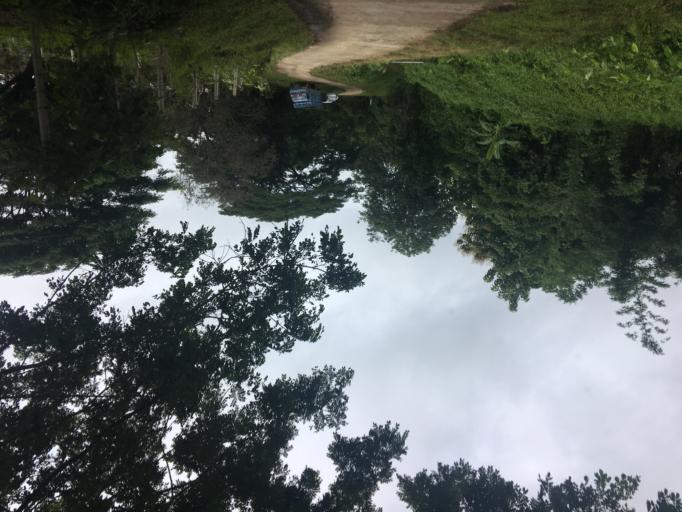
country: TH
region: Chiang Rai
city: Mae Lao
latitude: 19.6926
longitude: 99.6570
